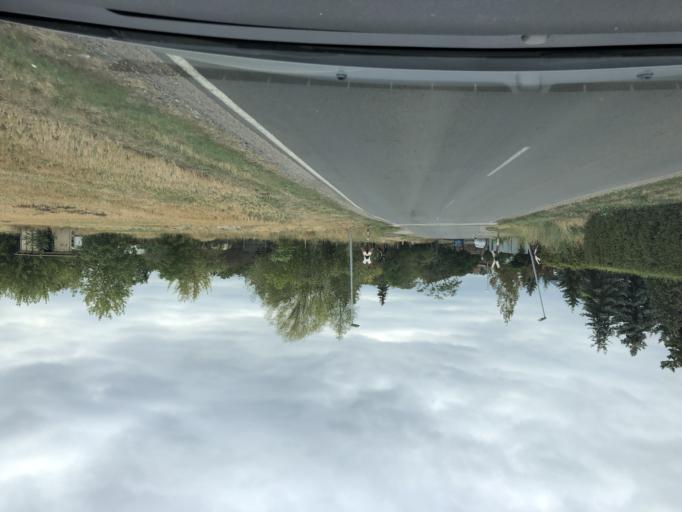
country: DE
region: Saxony-Anhalt
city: Zorbig
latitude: 51.6309
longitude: 12.1261
